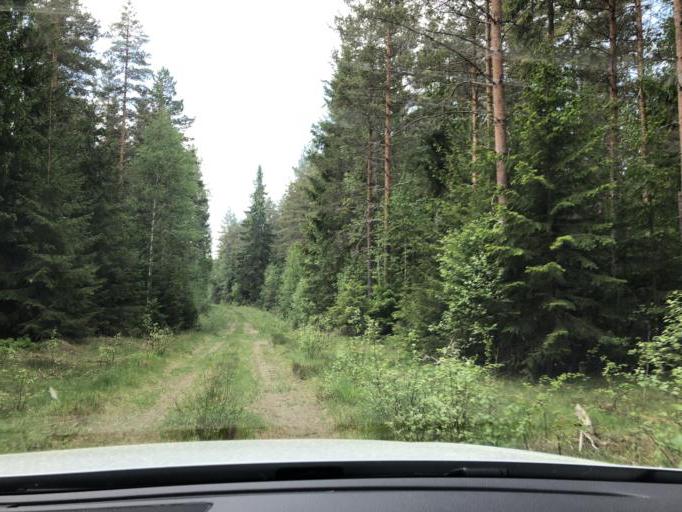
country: SE
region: Dalarna
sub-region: Avesta Kommun
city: Horndal
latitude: 60.2197
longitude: 16.5054
